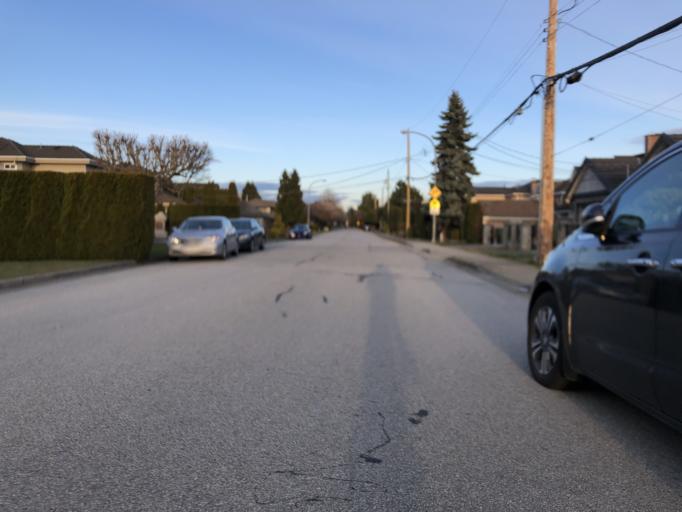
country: CA
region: British Columbia
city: Richmond
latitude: 49.1518
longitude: -123.1221
